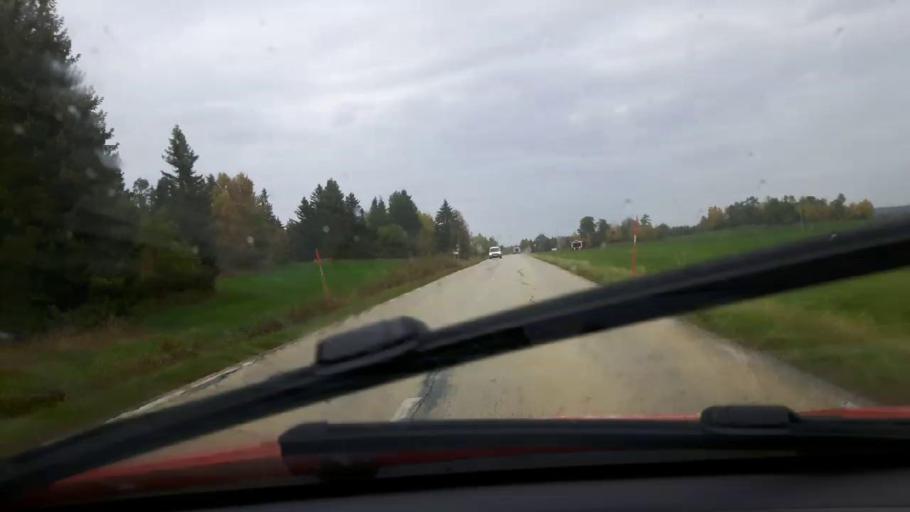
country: SE
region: Jaemtland
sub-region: Bergs Kommun
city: Hoverberg
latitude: 62.9436
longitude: 14.3358
